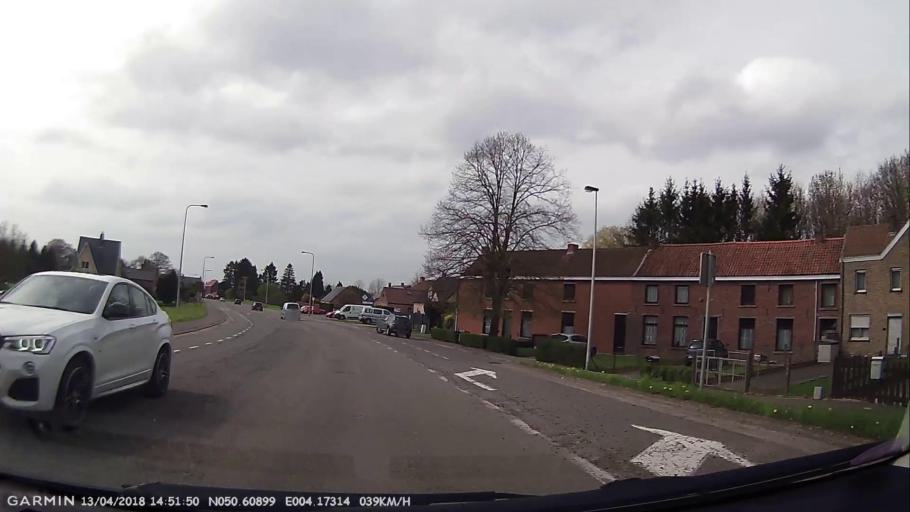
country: BE
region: Wallonia
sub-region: Province du Hainaut
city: Braine-le-Comte
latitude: 50.6090
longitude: 4.1733
